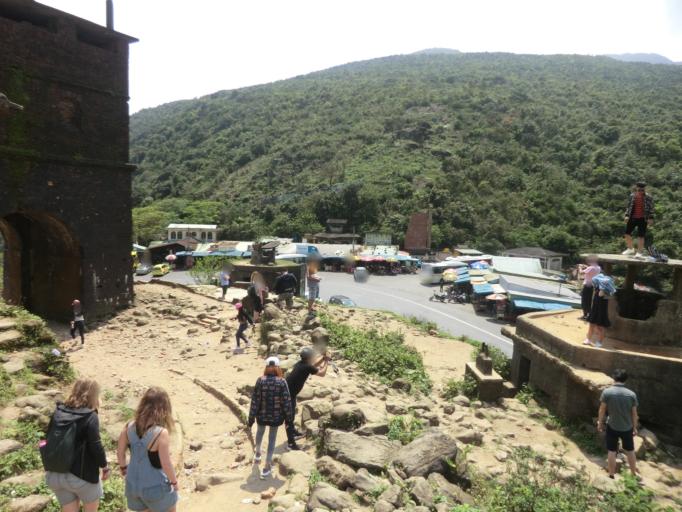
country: VN
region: Da Nang
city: Lien Chieu
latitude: 16.1878
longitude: 108.1312
